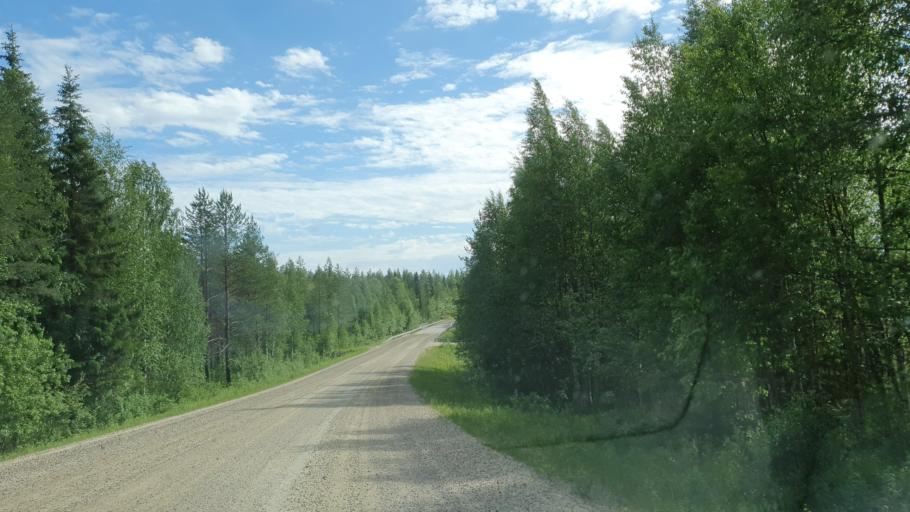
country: FI
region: Kainuu
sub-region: Kehys-Kainuu
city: Kuhmo
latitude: 64.4677
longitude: 29.5387
